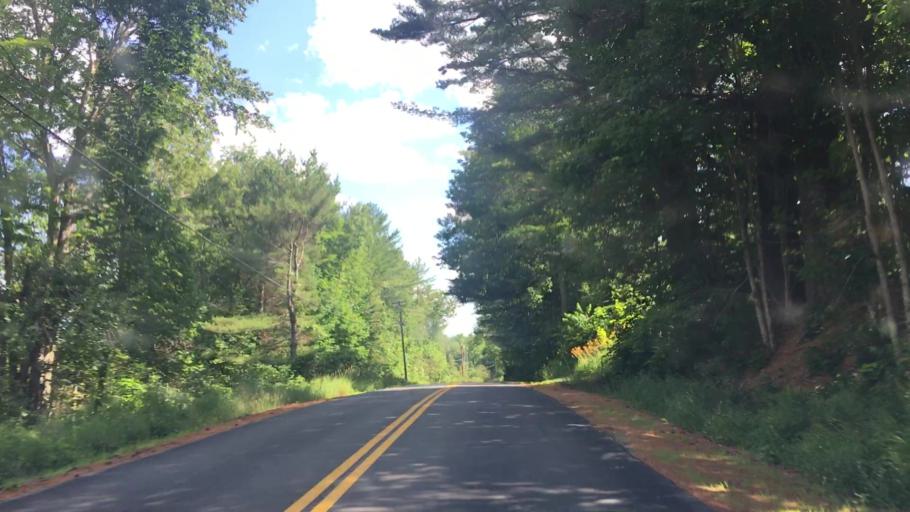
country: US
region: Maine
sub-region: Franklin County
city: Farmington
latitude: 44.6814
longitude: -70.1316
